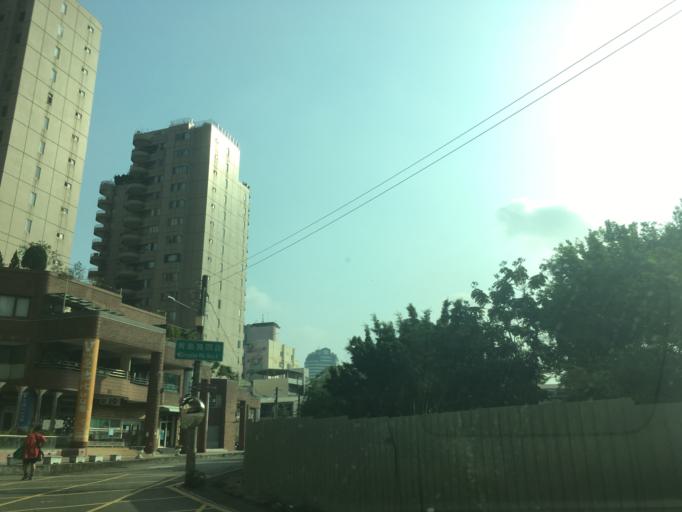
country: TW
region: Taiwan
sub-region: Taichung City
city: Taichung
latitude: 24.1659
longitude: 120.6922
